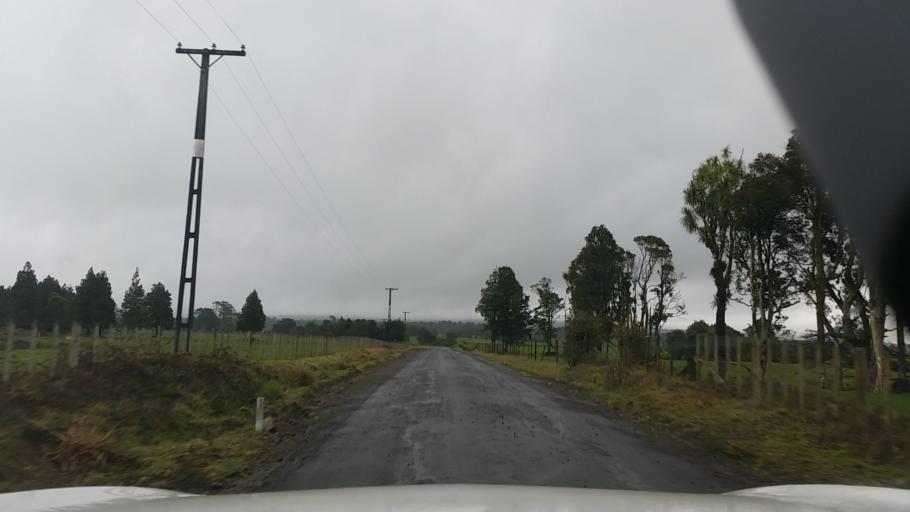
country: NZ
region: Taranaki
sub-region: South Taranaki District
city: Eltham
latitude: -39.2727
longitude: 174.1949
